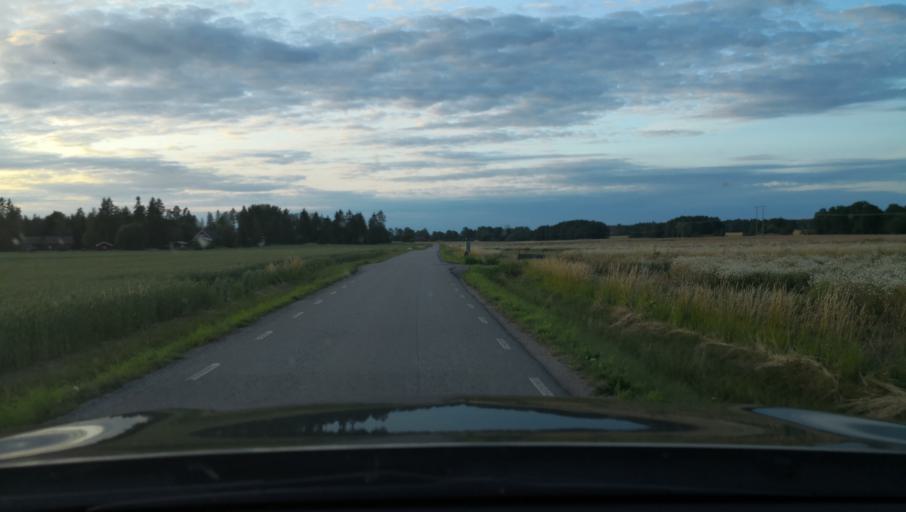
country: SE
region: Uppsala
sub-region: Uppsala Kommun
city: Vattholma
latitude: 60.0276
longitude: 17.6643
